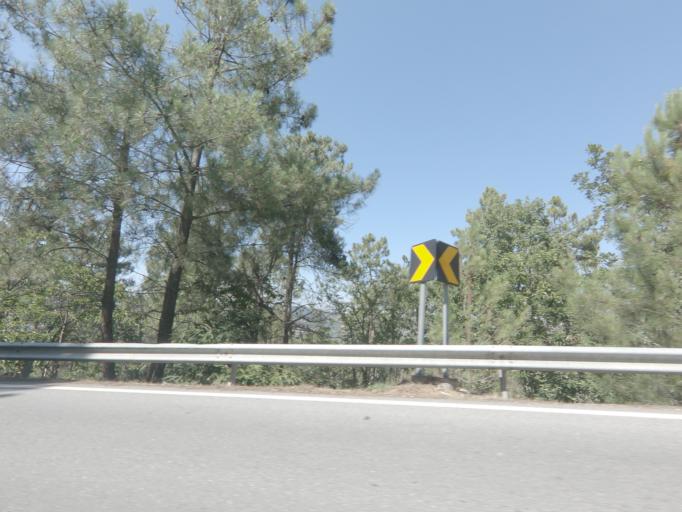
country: PT
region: Viseu
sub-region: Tarouca
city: Tarouca
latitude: 41.0389
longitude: -7.7328
